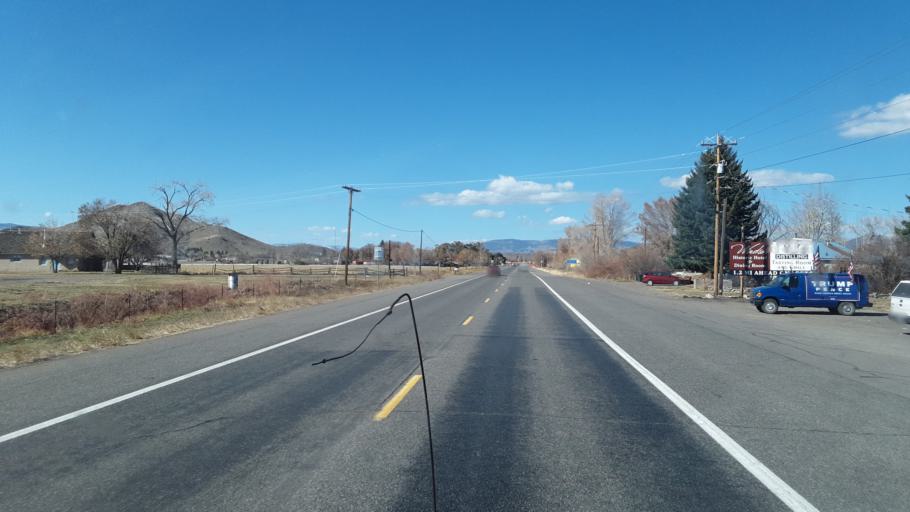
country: US
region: Colorado
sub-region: Rio Grande County
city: Del Norte
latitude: 37.6759
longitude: -106.3323
